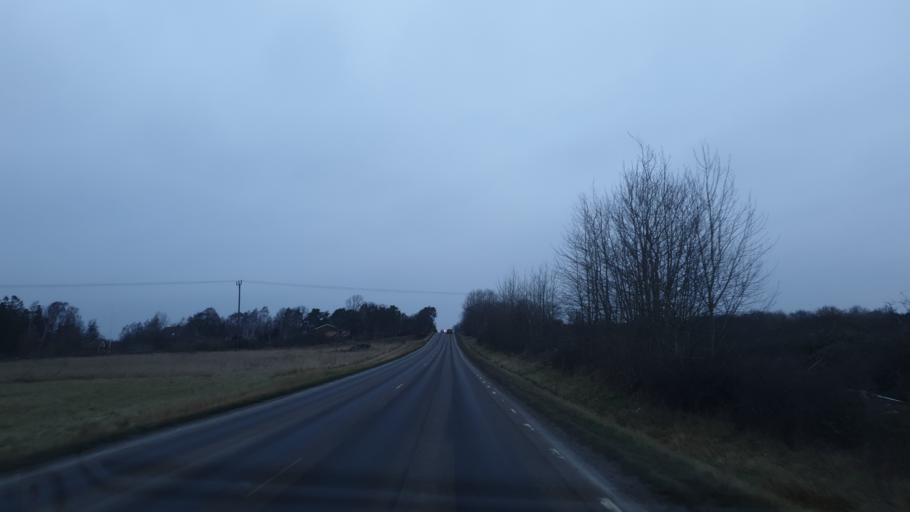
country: SE
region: Blekinge
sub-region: Karlskrona Kommun
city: Jaemjoe
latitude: 56.1475
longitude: 15.7589
